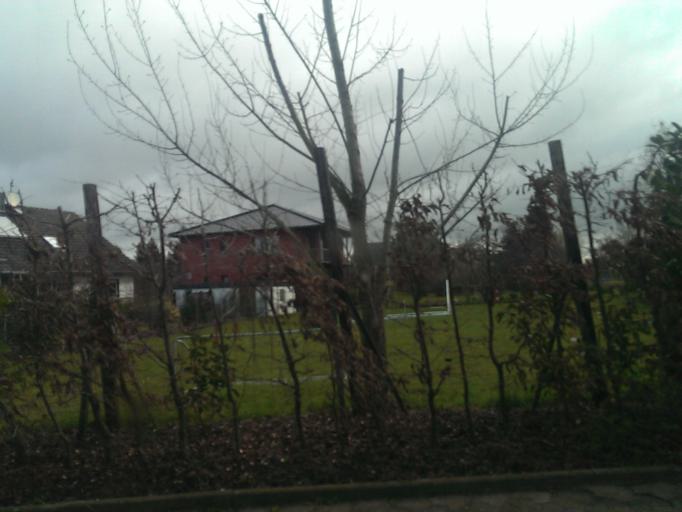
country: DE
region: Lower Saxony
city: Schellerten
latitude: 52.1532
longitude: 10.0800
